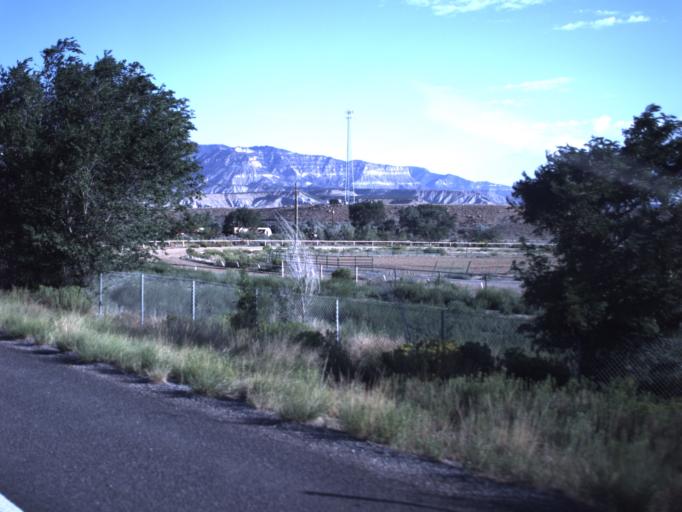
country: US
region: Utah
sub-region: Emery County
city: Huntington
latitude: 39.3381
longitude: -110.9730
